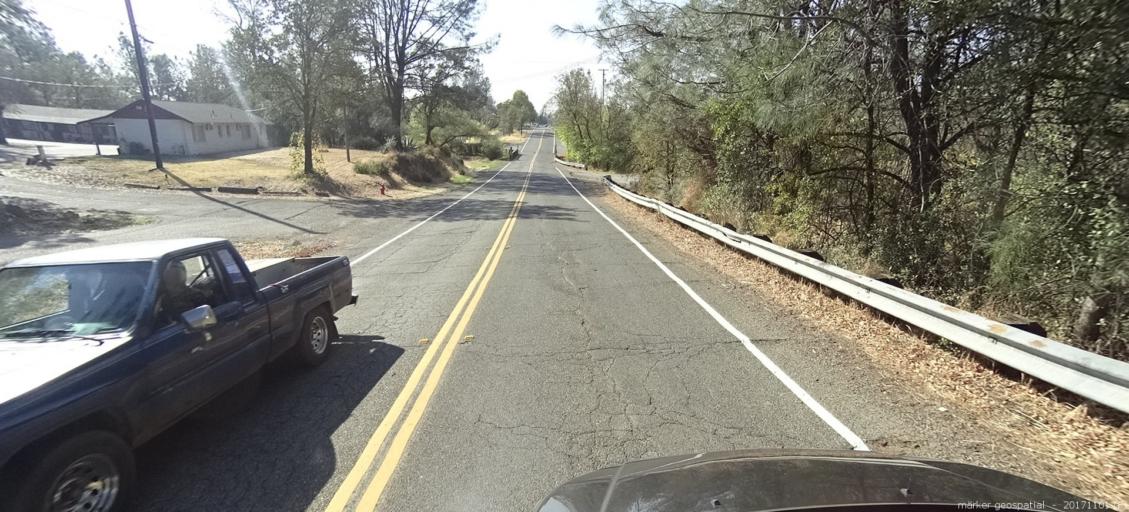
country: US
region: California
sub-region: Shasta County
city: Shasta Lake
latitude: 40.6826
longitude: -122.3487
